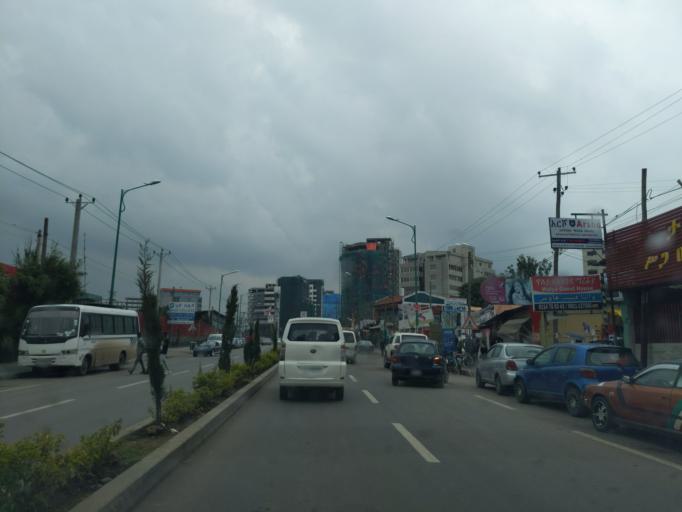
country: ET
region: Adis Abeba
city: Addis Ababa
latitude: 8.9980
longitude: 38.7669
